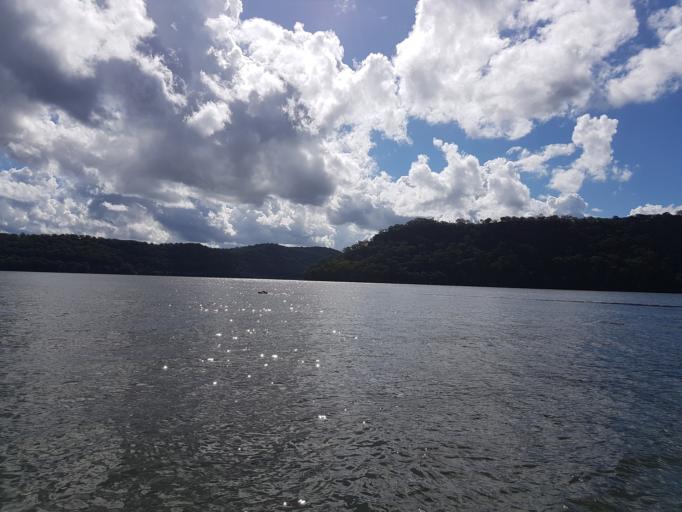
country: AU
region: New South Wales
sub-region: Gosford Shire
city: Umina
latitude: -33.5360
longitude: 151.2416
